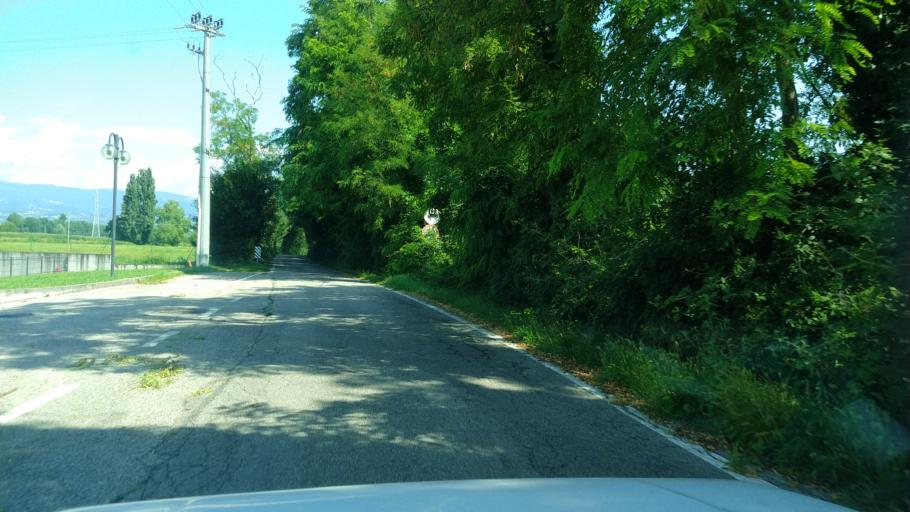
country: IT
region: Veneto
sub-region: Provincia di Vicenza
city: Tezze
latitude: 45.6837
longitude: 11.6816
